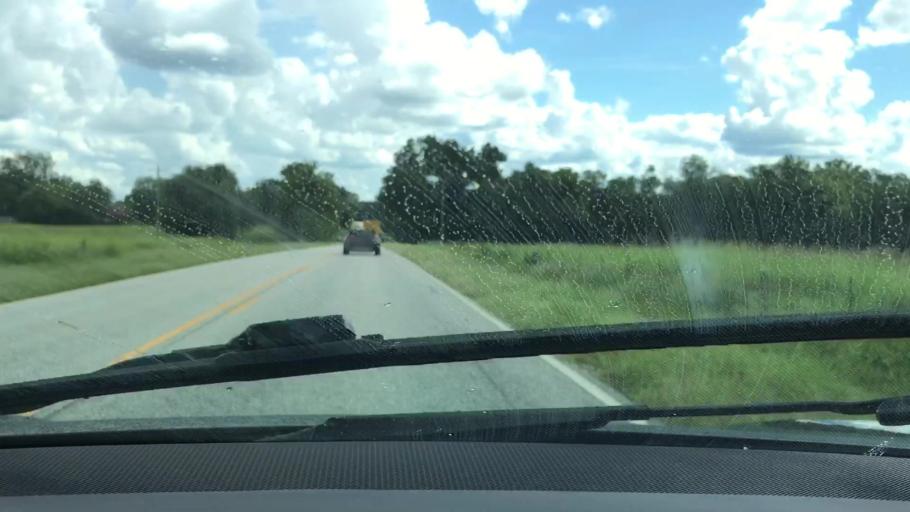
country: US
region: Alabama
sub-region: Montgomery County
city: Pike Road
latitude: 32.2386
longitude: -86.0932
